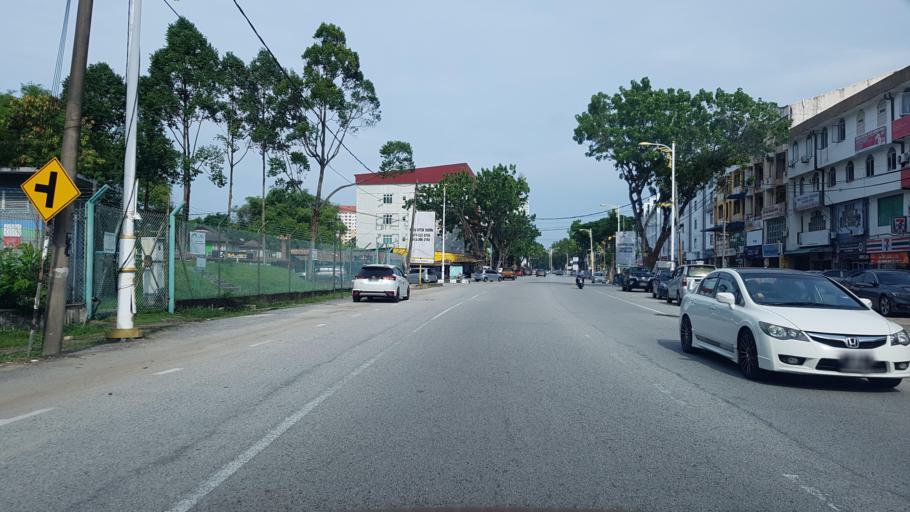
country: MY
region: Terengganu
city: Kuala Terengganu
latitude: 5.3336
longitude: 103.1413
